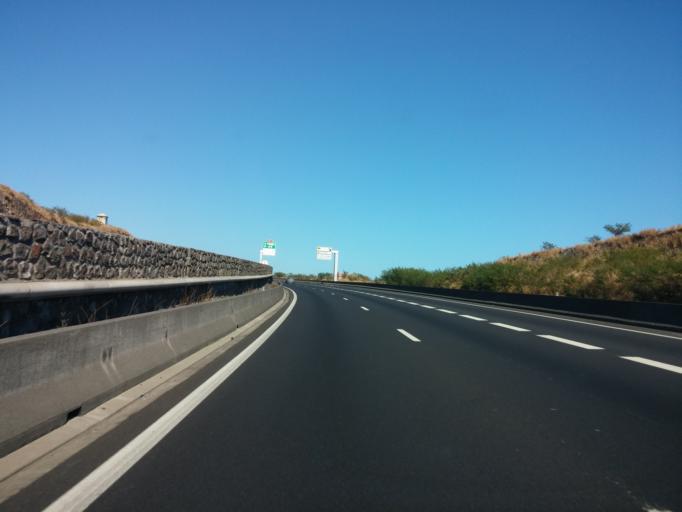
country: RE
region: Reunion
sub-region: Reunion
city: Saint-Paul
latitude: -21.0186
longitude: 55.2594
